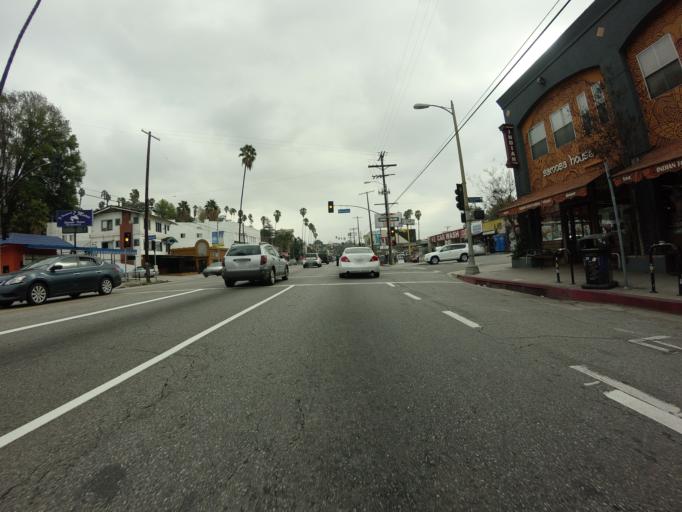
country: US
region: California
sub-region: Los Angeles County
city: Silver Lake
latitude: 34.0857
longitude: -118.2750
